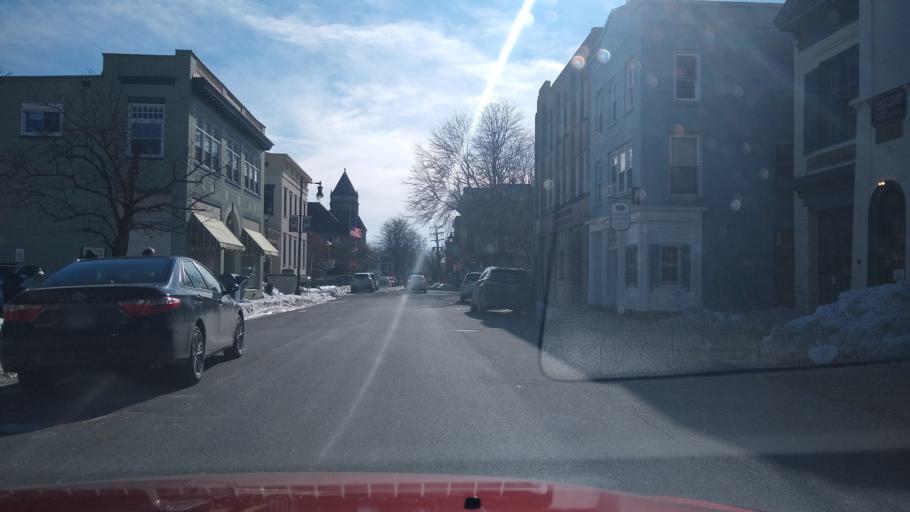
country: US
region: New York
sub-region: Ulster County
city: Kingston
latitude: 41.9335
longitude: -74.0185
